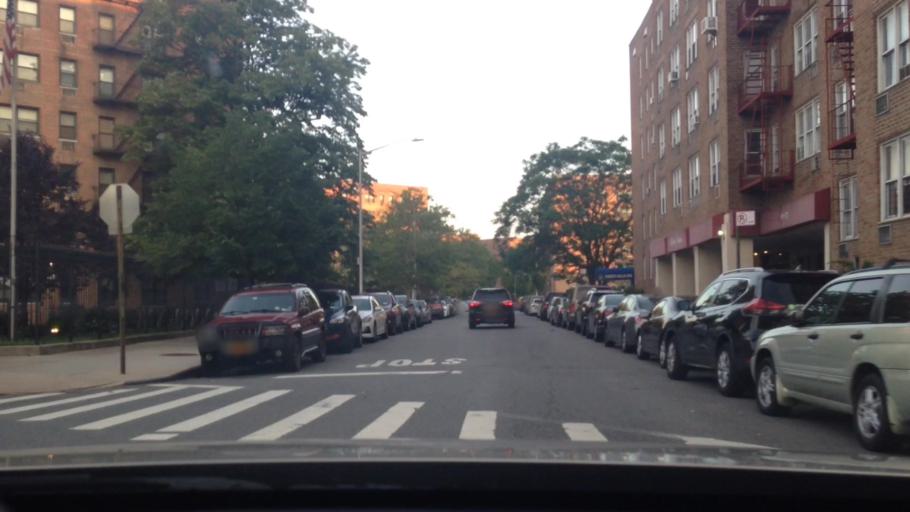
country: US
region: New York
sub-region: Queens County
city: Borough of Queens
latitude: 40.7373
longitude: -73.8560
